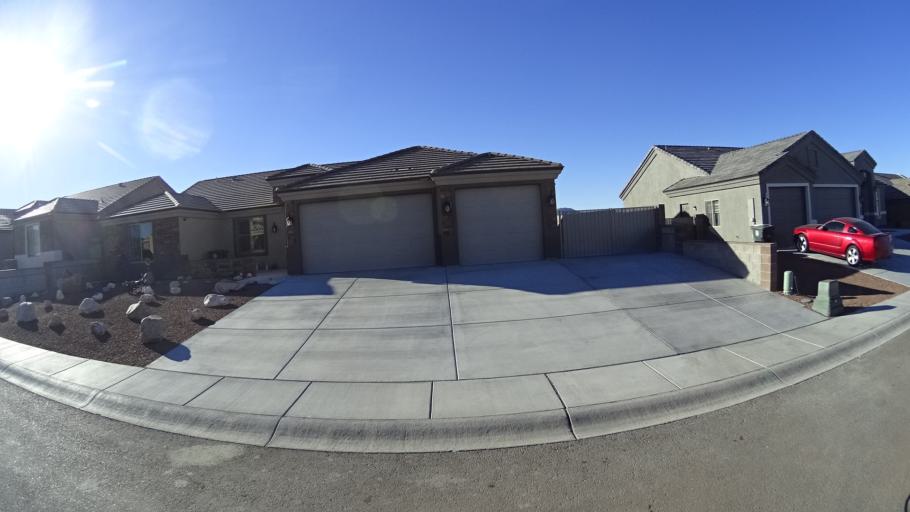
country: US
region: Arizona
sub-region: Mohave County
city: Kingman
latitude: 35.1914
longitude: -113.9963
